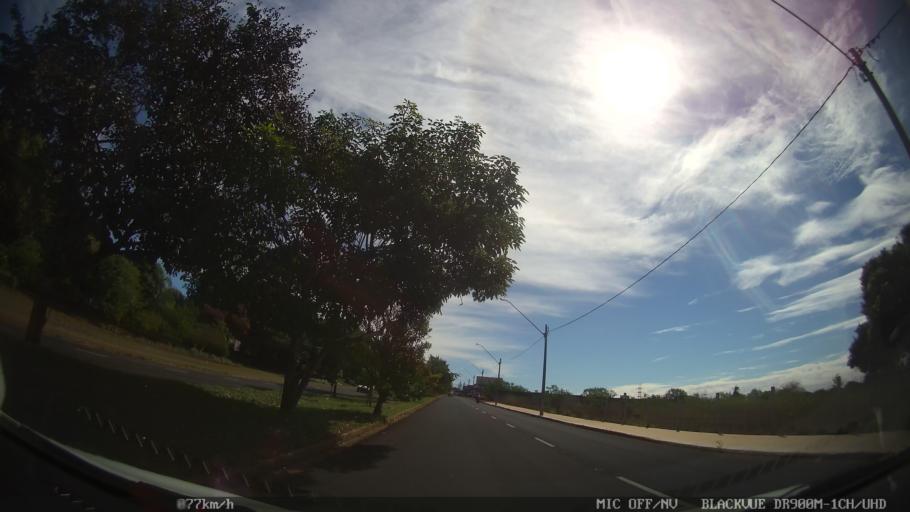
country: BR
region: Sao Paulo
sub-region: Sao Jose Do Rio Preto
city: Sao Jose do Rio Preto
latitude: -20.8348
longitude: -49.3472
